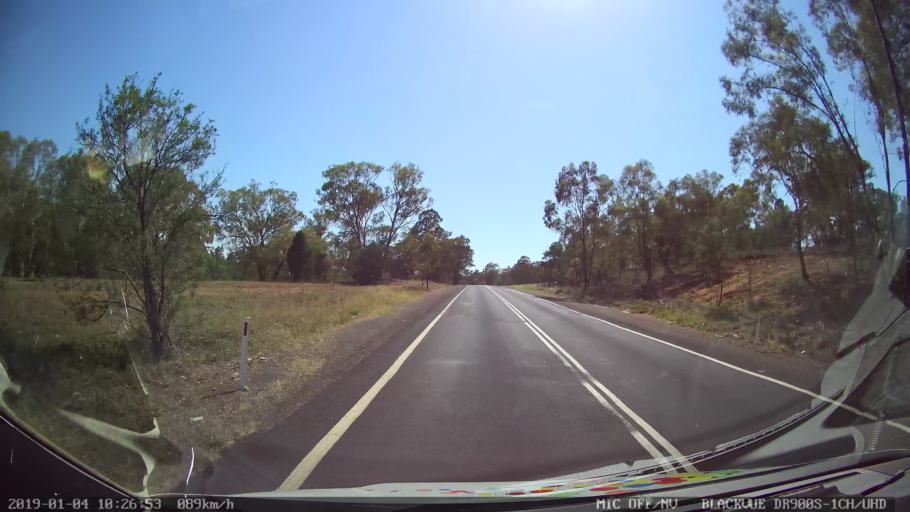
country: AU
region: New South Wales
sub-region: Cabonne
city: Canowindra
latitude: -33.3746
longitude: 148.5920
